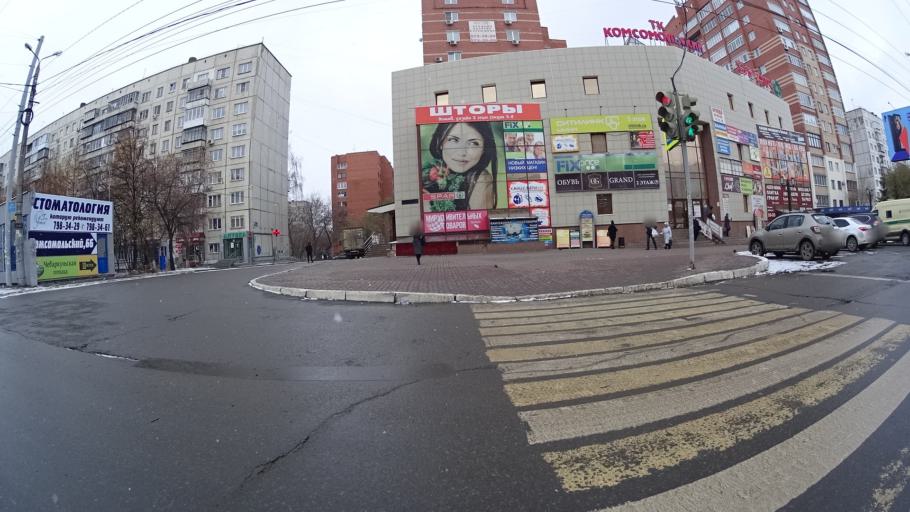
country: RU
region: Chelyabinsk
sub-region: Gorod Chelyabinsk
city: Chelyabinsk
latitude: 55.1946
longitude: 61.3261
